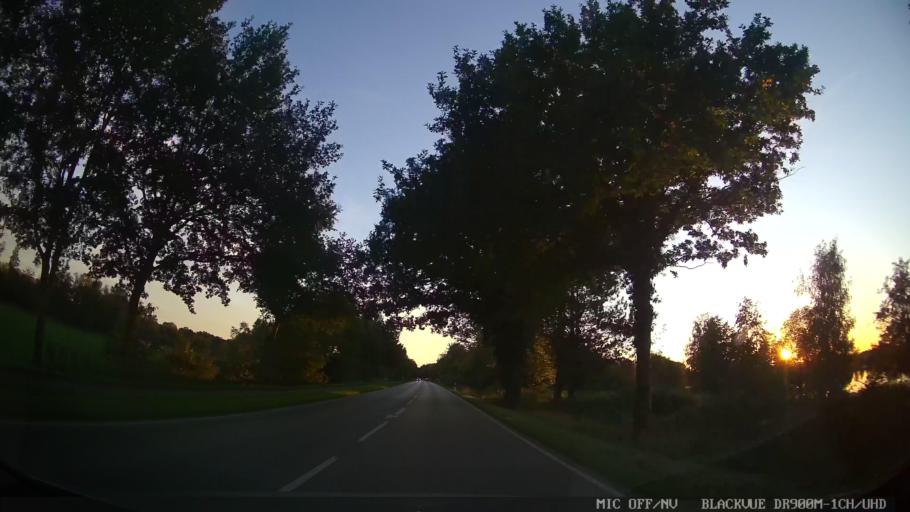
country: DE
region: Schleswig-Holstein
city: Susel
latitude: 54.0775
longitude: 10.6914
